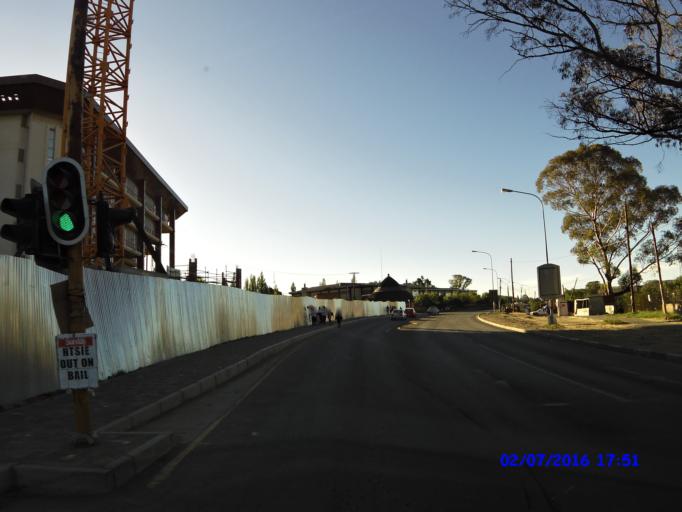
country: LS
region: Maseru
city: Maseru
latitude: -29.3127
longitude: 27.4902
